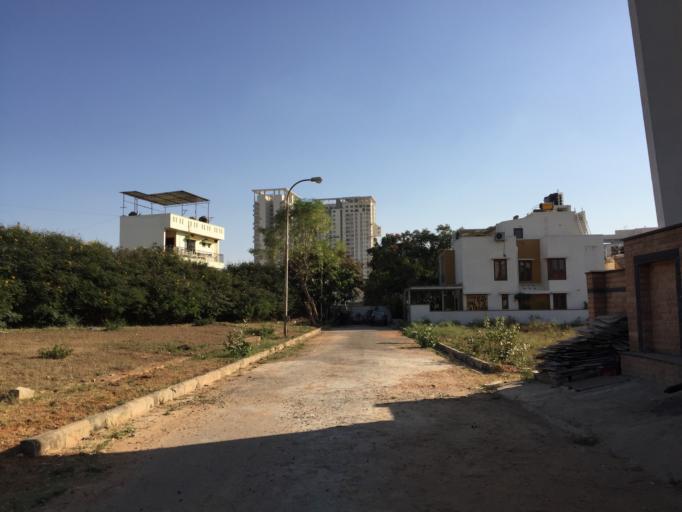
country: IN
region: Karnataka
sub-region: Bangalore Urban
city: Yelahanka
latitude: 13.0534
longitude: 77.6252
